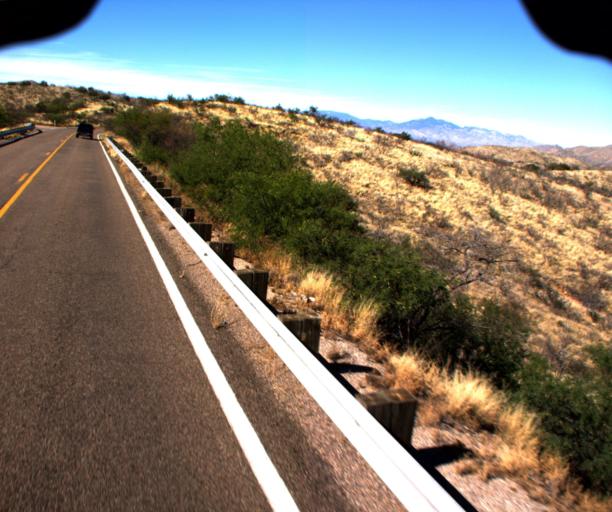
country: US
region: Arizona
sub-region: Pima County
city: Corona de Tucson
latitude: 31.8392
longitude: -110.7016
